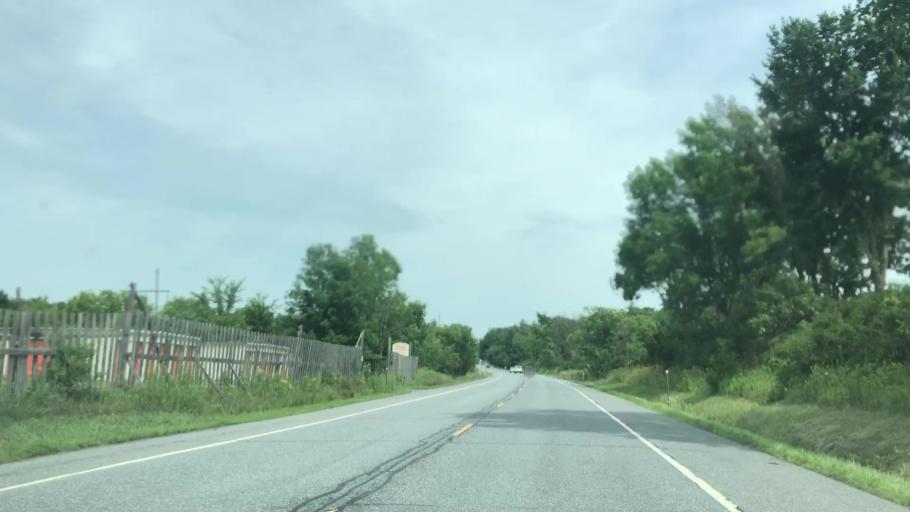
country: US
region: New York
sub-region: Washington County
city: Whitehall
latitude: 43.5511
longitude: -73.3644
